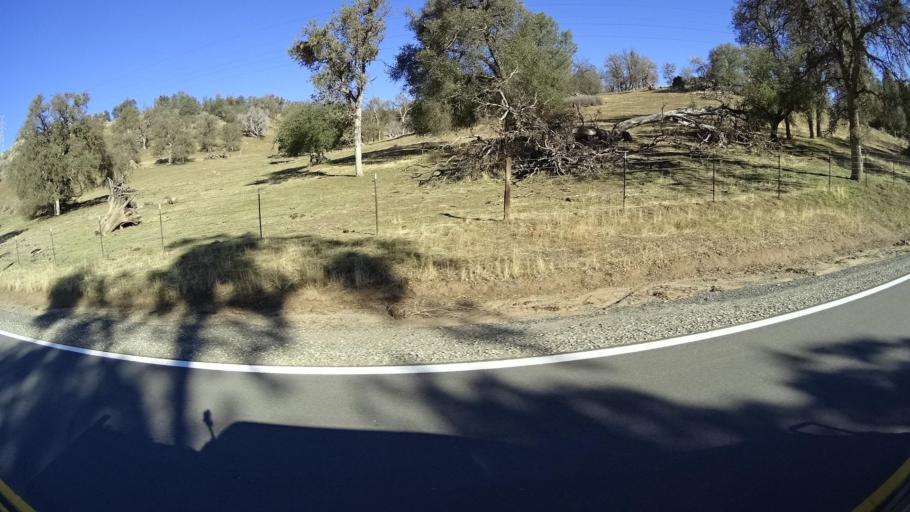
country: US
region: California
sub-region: Kern County
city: Alta Sierra
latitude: 35.7053
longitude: -118.7506
